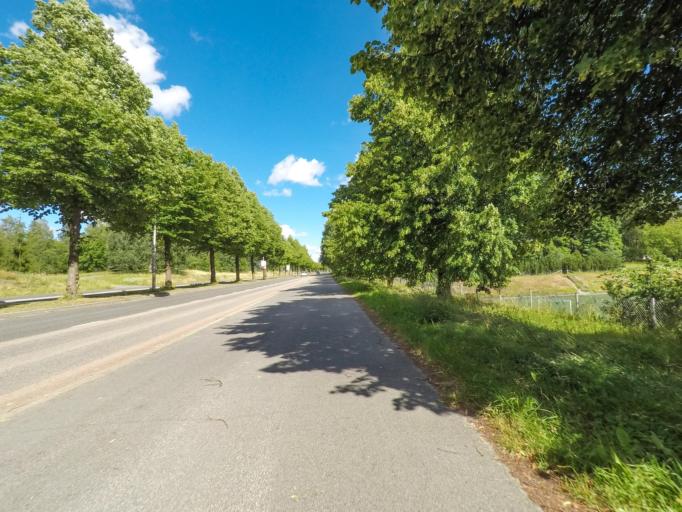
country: FI
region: South Karelia
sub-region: Lappeenranta
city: Lappeenranta
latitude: 61.0607
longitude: 28.2066
